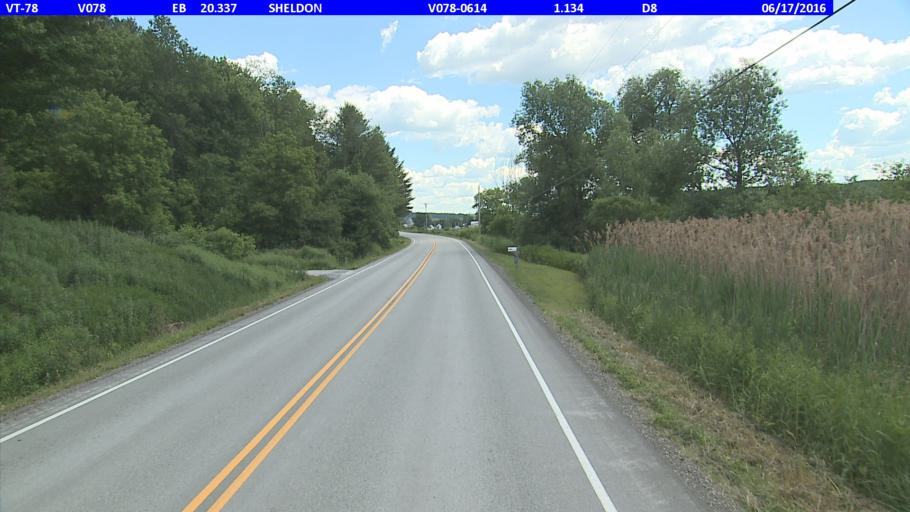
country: US
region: Vermont
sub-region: Franklin County
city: Enosburg Falls
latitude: 44.9113
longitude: -72.9552
